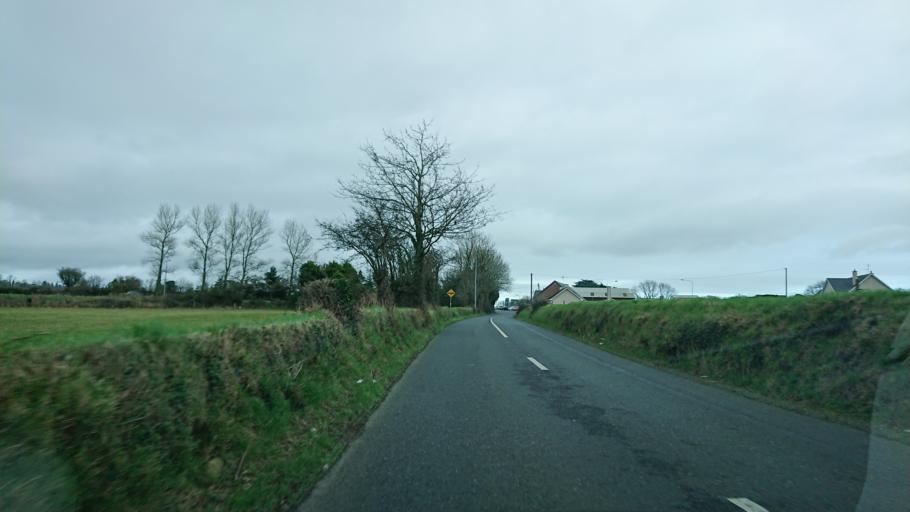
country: IE
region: Leinster
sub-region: Kilkenny
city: Mooncoin
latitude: 52.2264
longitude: -7.2349
